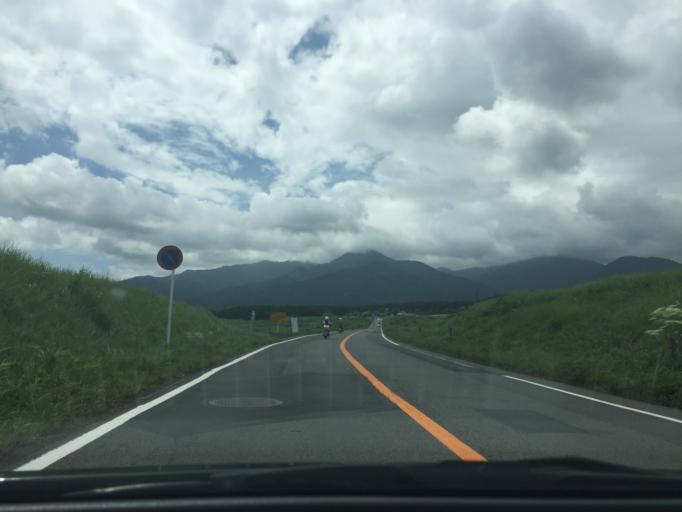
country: JP
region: Shizuoka
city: Gotemba
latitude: 35.2651
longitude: 138.8686
